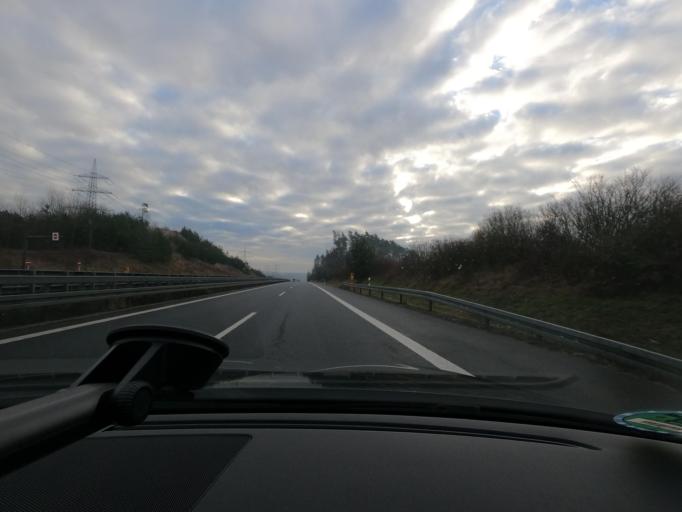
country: DE
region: Bavaria
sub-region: Upper Franconia
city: Rodental
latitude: 50.2507
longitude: 11.0314
